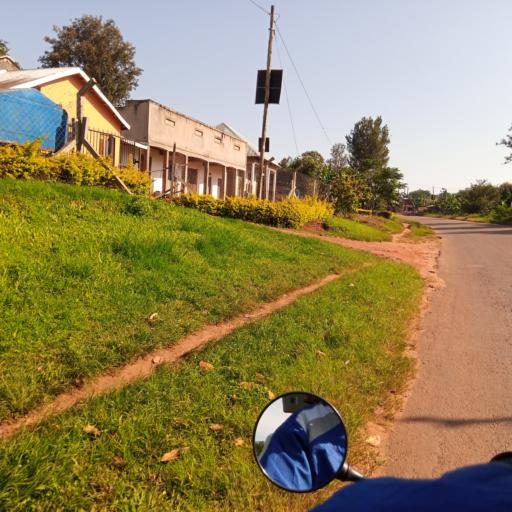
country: UG
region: Central Region
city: Masaka
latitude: -0.4493
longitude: 31.6685
